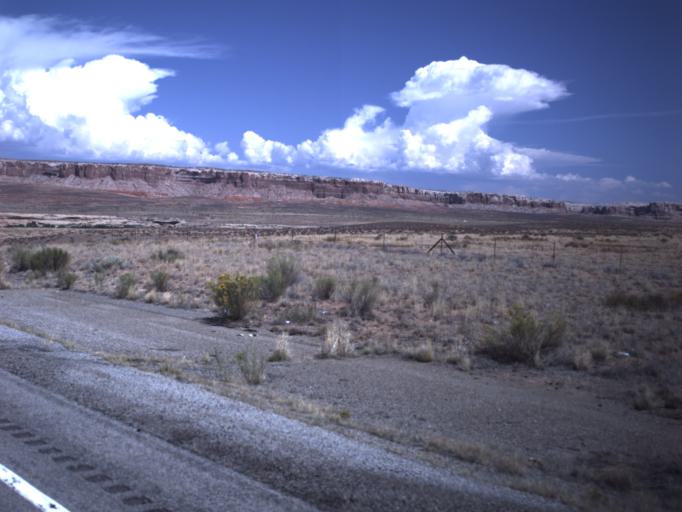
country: US
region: Utah
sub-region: San Juan County
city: Blanding
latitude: 37.2511
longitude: -109.6121
